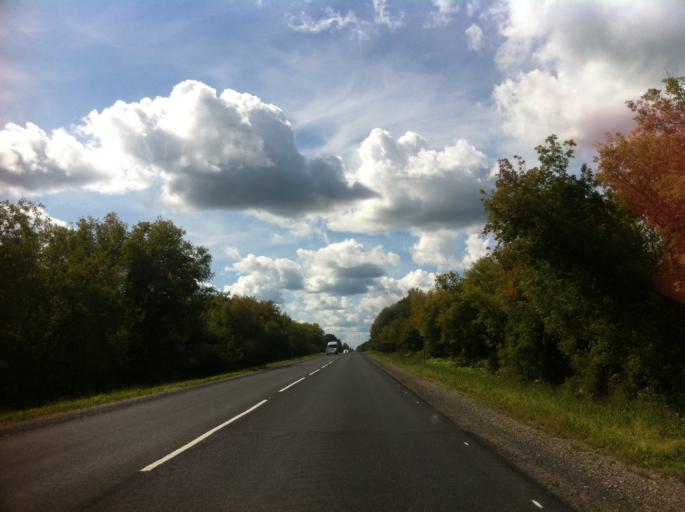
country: RU
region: Pskov
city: Izborsk
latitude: 57.7296
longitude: 27.9690
